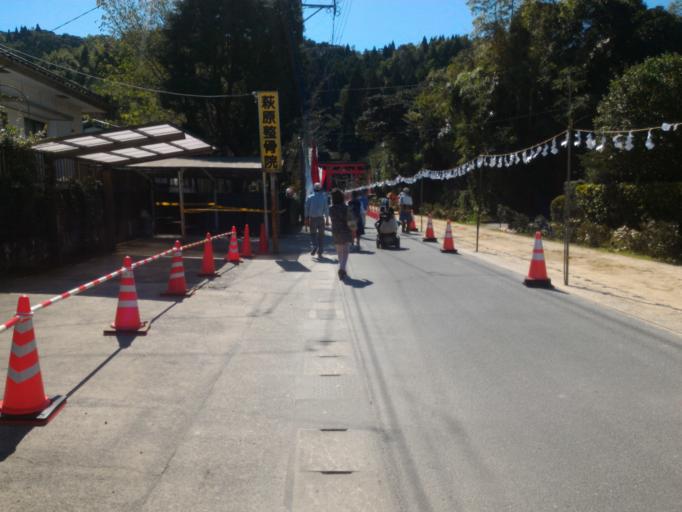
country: JP
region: Kagoshima
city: Kanoya
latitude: 31.3446
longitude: 130.9471
